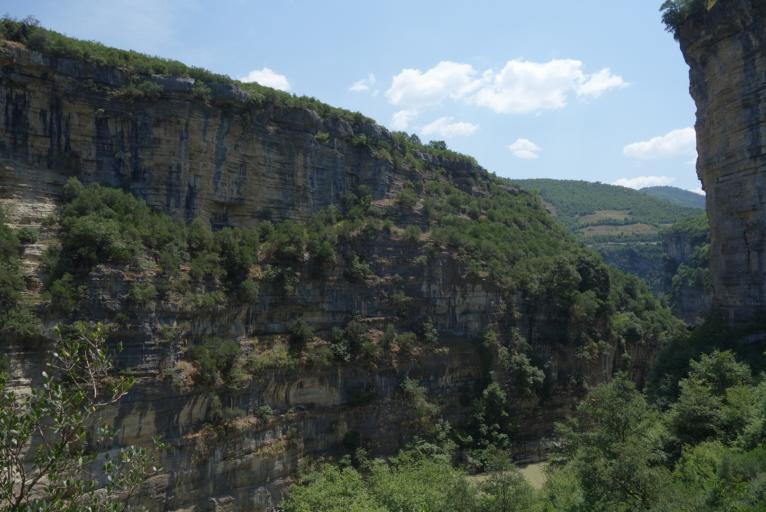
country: AL
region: Berat
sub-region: Rrethi i Skraparit
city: Cepan
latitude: 40.4660
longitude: 20.2597
